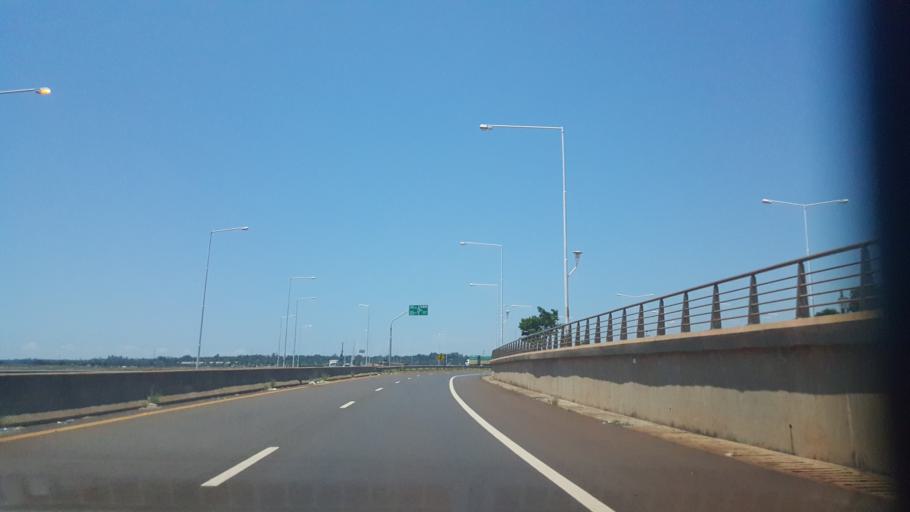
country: AR
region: Misiones
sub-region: Departamento de Capital
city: Posadas
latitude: -27.4015
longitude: -55.8920
